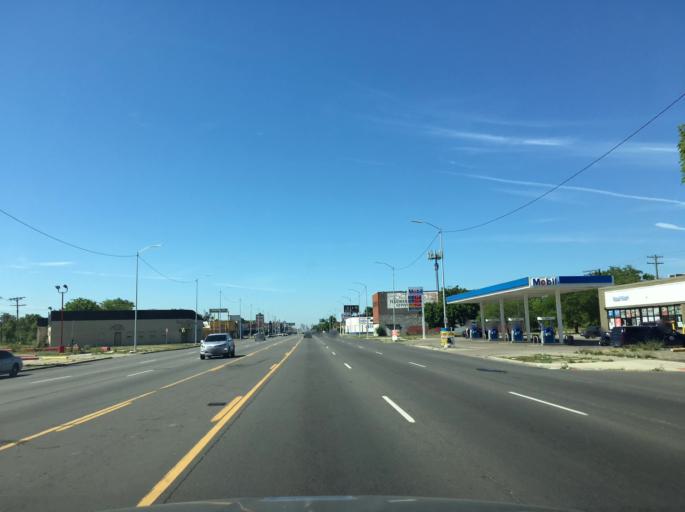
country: US
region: Michigan
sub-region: Macomb County
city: Eastpointe
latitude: 42.4240
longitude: -82.9851
